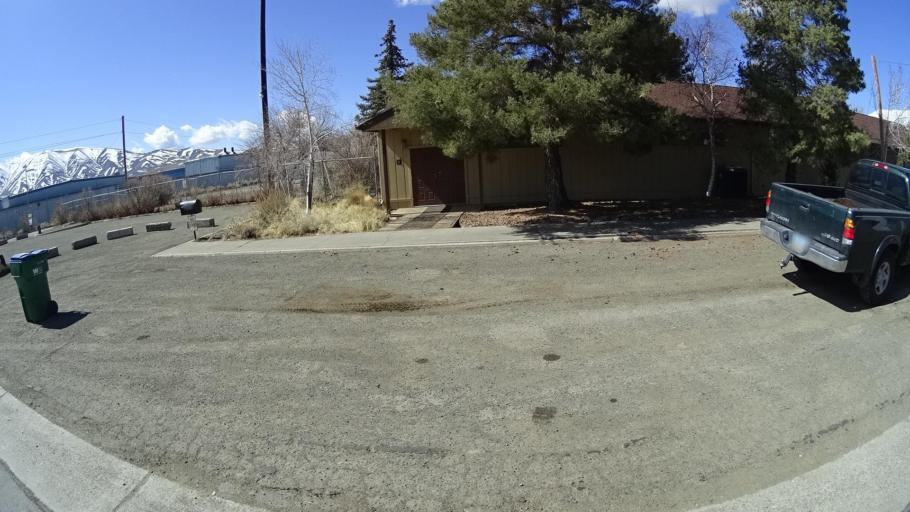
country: US
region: Nevada
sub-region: Washoe County
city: Lemmon Valley
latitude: 39.6556
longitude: -119.8834
